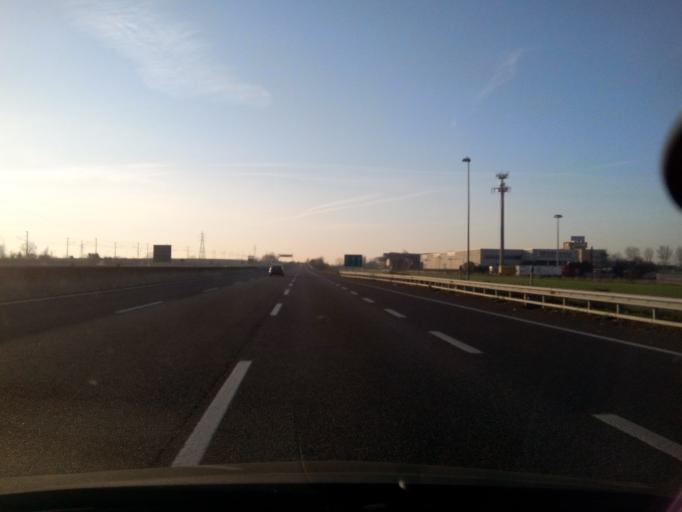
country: IT
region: Lombardy
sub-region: Provincia di Lodi
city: Ospedaletto Lodigiano
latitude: 45.1760
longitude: 9.5855
